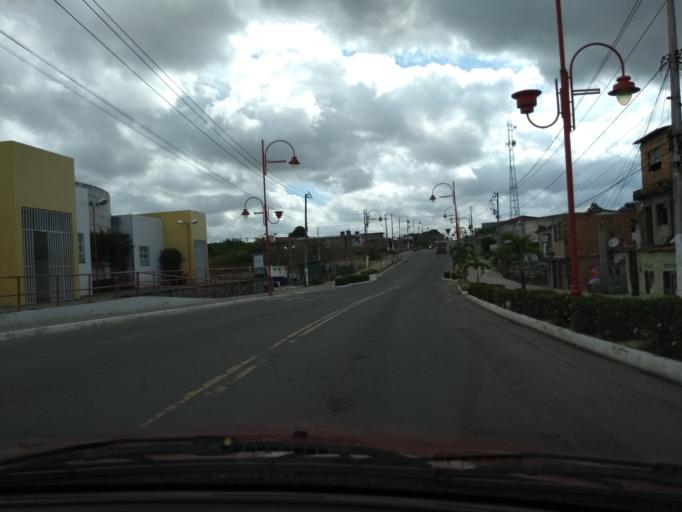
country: BR
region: Bahia
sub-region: Sao Francisco Do Conde
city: Sao Francisco do Conde
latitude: -12.6164
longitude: -38.6658
